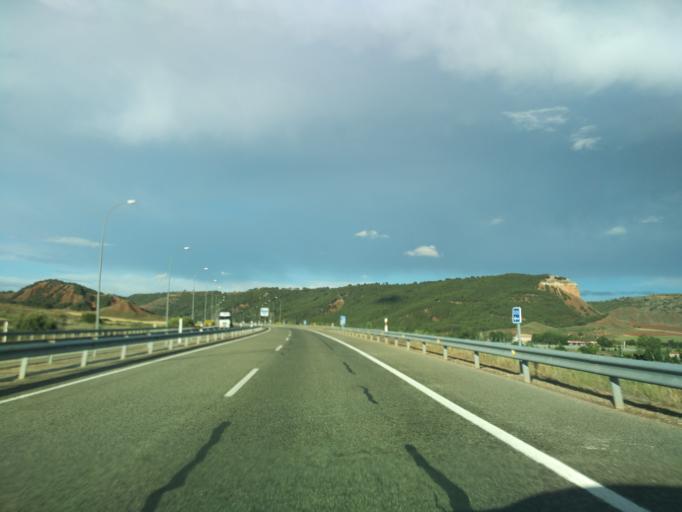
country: ES
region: Castille-La Mancha
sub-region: Provincia de Guadalajara
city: Tortola de Henares
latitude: 40.6594
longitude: -3.1284
